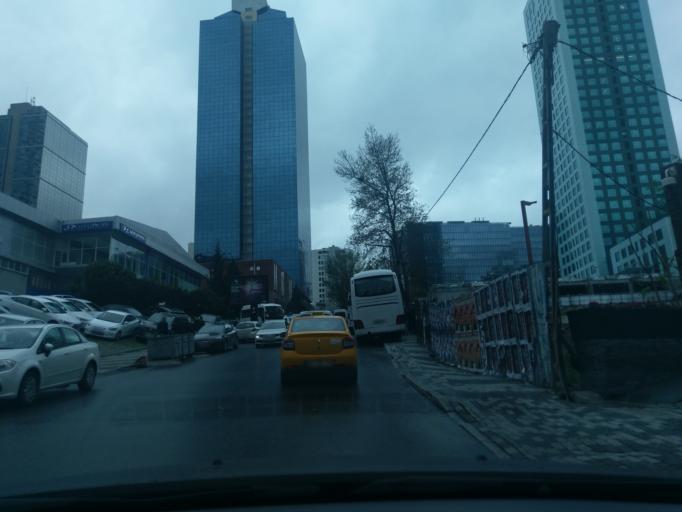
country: TR
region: Istanbul
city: Sisli
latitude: 41.1116
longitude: 29.0202
